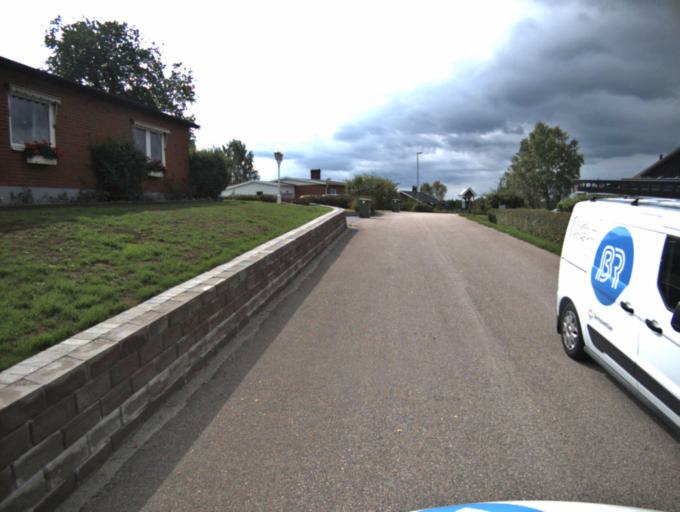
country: SE
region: Vaestra Goetaland
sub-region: Ulricehamns Kommun
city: Ulricehamn
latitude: 57.8982
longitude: 13.3537
